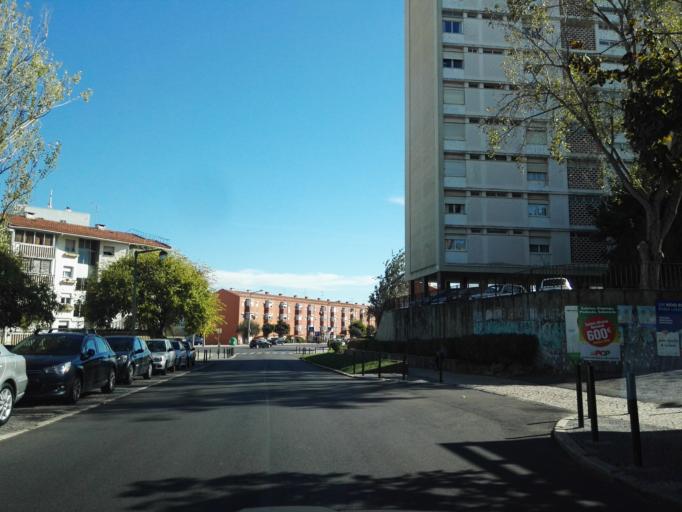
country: PT
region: Lisbon
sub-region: Loures
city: Moscavide
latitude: 38.7753
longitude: -9.1123
